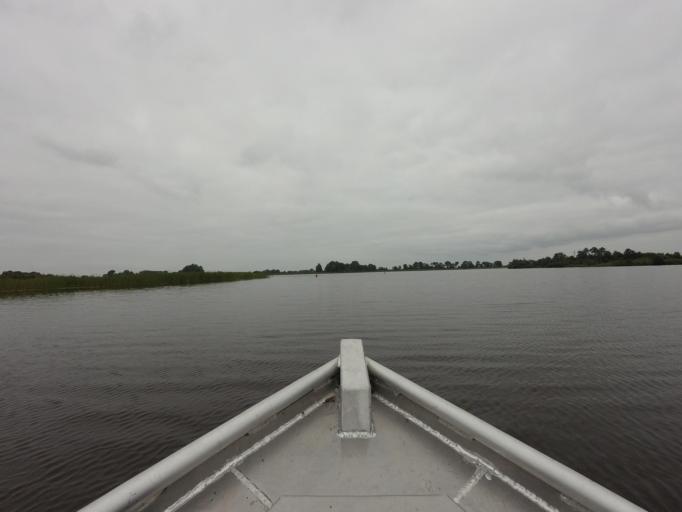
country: NL
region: Overijssel
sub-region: Gemeente Steenwijkerland
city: Blokzijl
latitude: 52.7328
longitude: 5.9938
